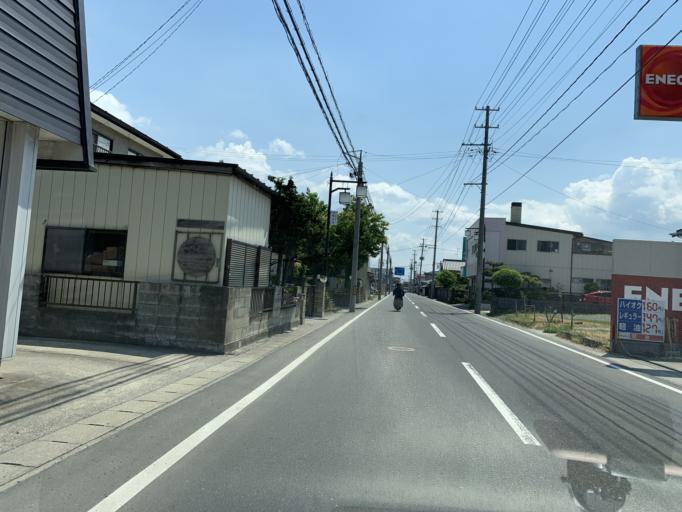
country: JP
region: Miyagi
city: Kogota
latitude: 38.5596
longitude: 141.0530
